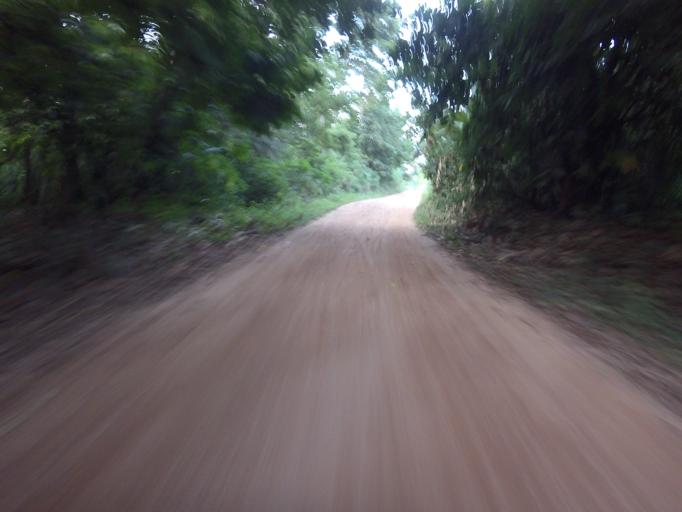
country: GH
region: Volta
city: Kpandu
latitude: 6.8874
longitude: 0.4374
